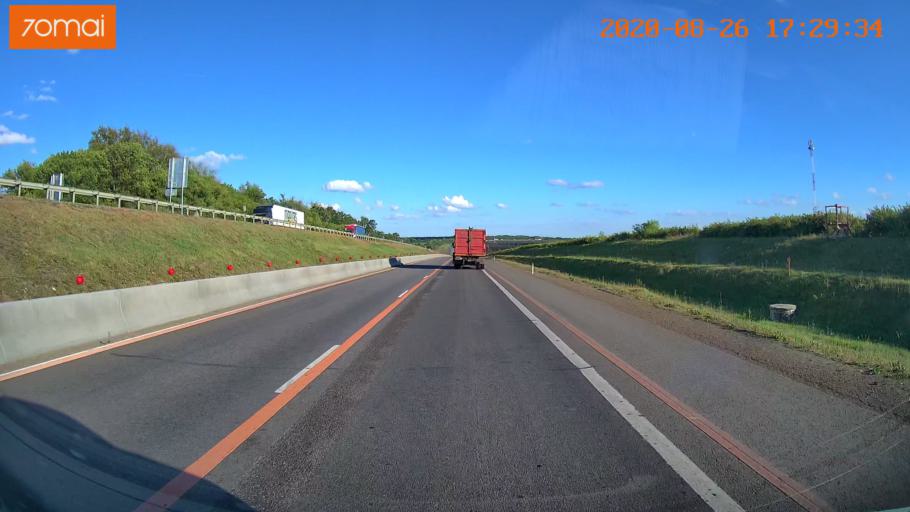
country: RU
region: Tula
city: Kazachka
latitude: 53.4529
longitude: 38.1540
